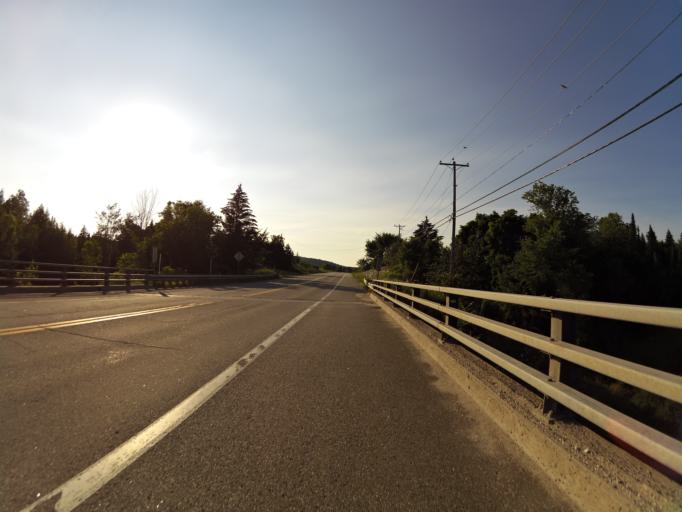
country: CA
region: Quebec
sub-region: Outaouais
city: Wakefield
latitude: 45.5963
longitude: -75.8962
